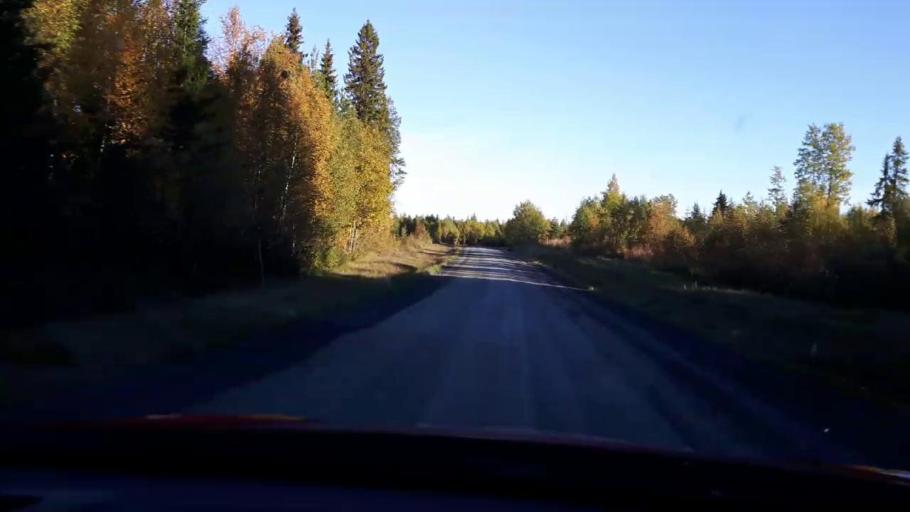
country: SE
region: Jaemtland
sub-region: OEstersunds Kommun
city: Lit
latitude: 63.6669
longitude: 14.7084
